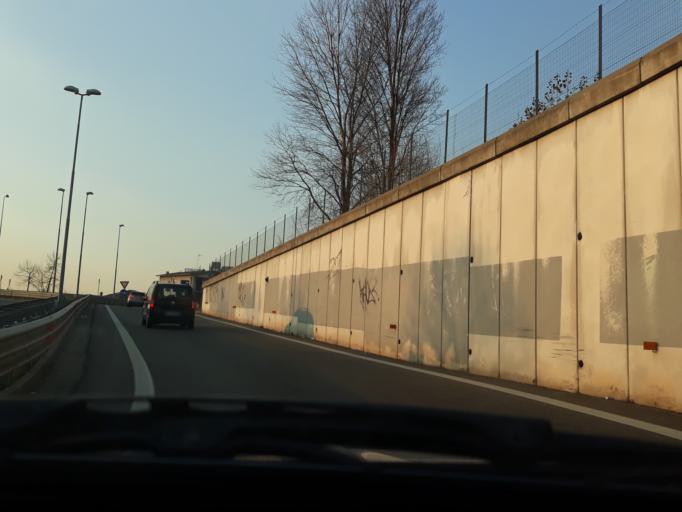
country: IT
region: Lombardy
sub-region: Citta metropolitana di Milano
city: Cinisello Balsamo
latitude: 45.5607
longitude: 9.2435
